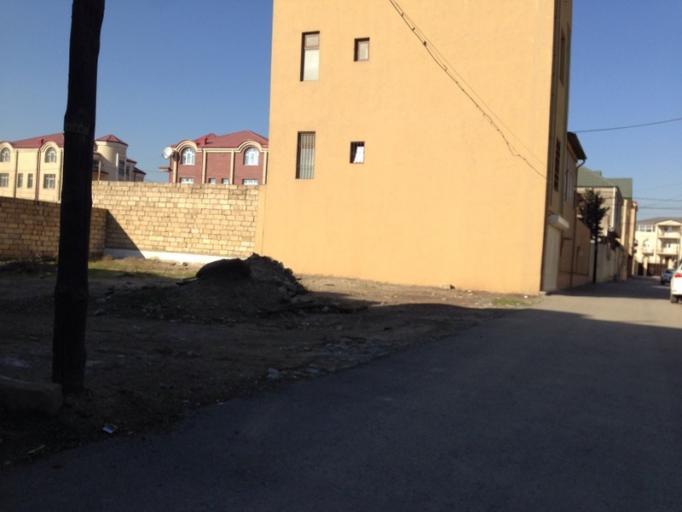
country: AZ
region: Baki
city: Baku
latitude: 40.4208
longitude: 49.8659
